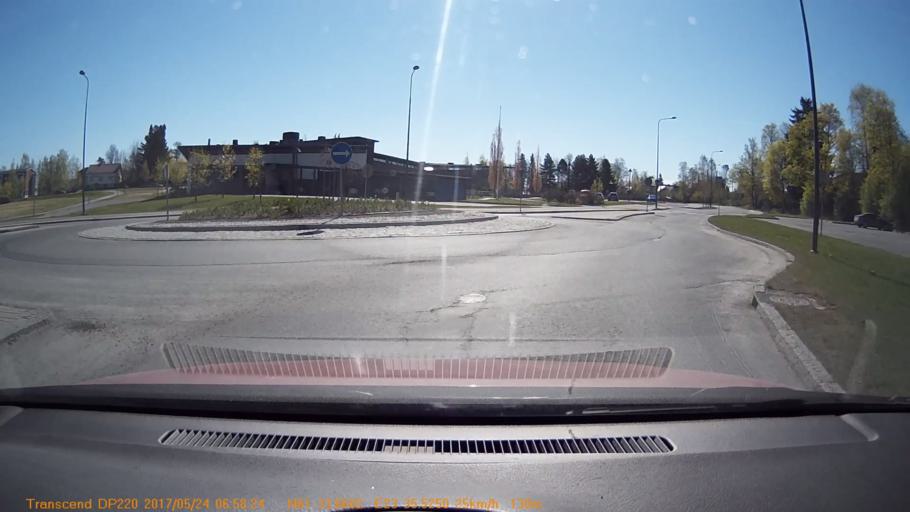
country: FI
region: Pirkanmaa
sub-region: Tampere
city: Yloejaervi
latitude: 61.5606
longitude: 23.5913
